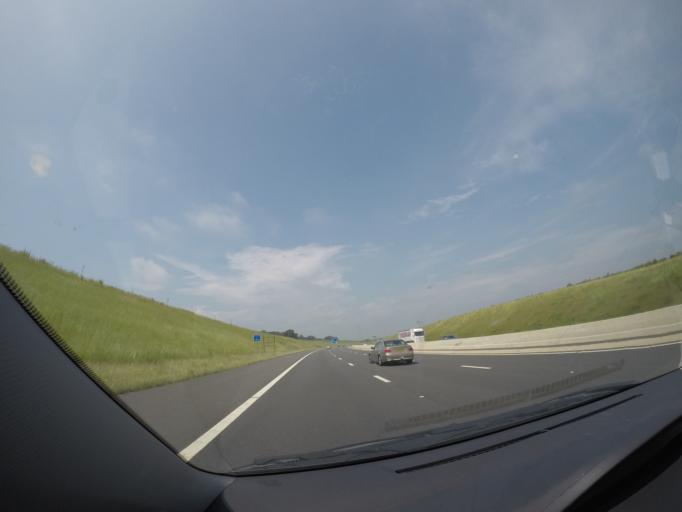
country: GB
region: England
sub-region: North Yorkshire
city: Catterick
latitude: 54.3621
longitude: -1.6266
